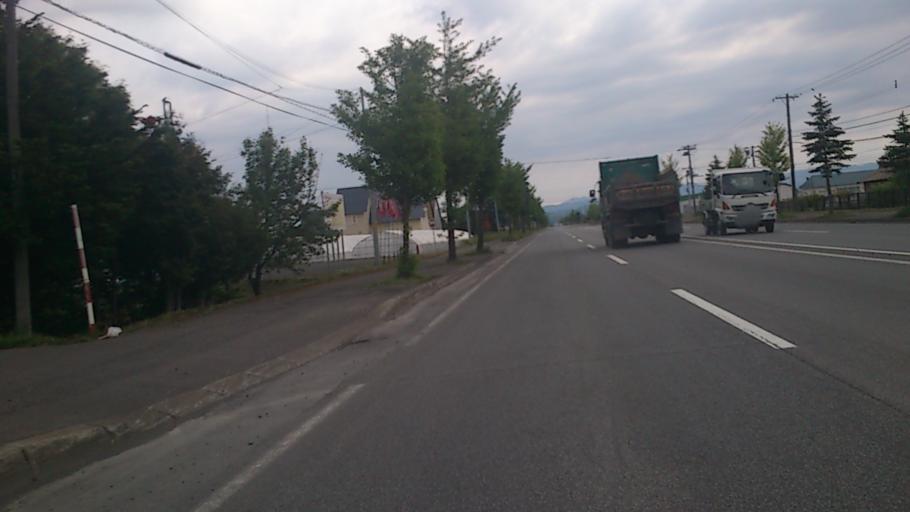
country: JP
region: Hokkaido
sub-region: Asahikawa-shi
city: Asahikawa
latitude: 43.8358
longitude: 142.4743
